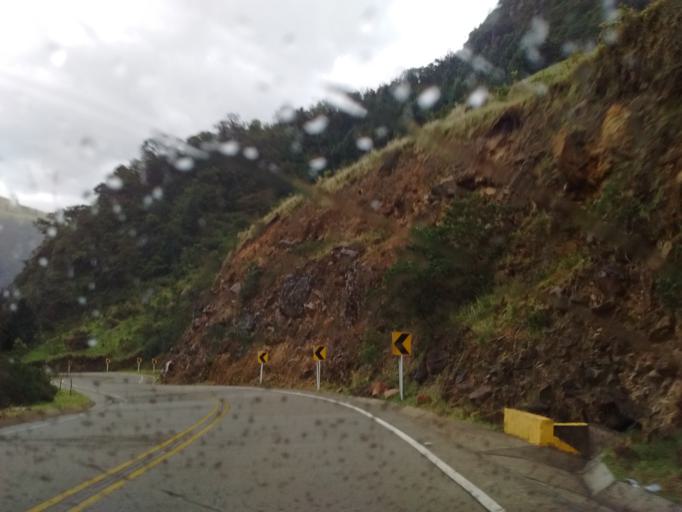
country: CO
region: Cauca
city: Paispamba
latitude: 2.2976
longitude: -76.5109
